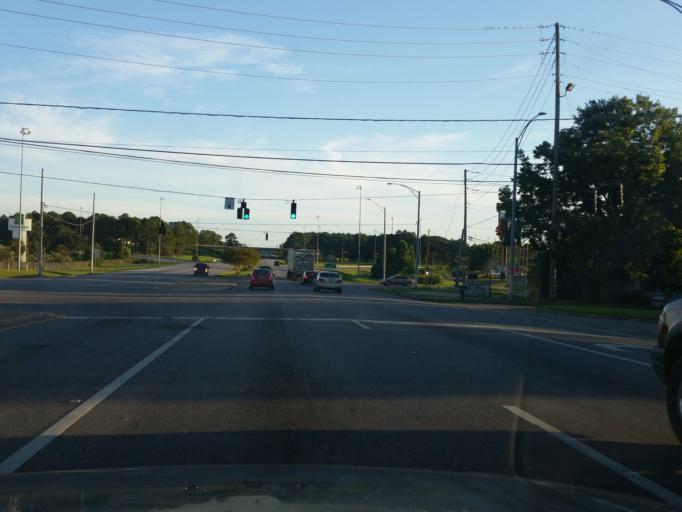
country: US
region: Alabama
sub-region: Mobile County
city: Tillmans Corner
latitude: 30.5864
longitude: -88.1699
